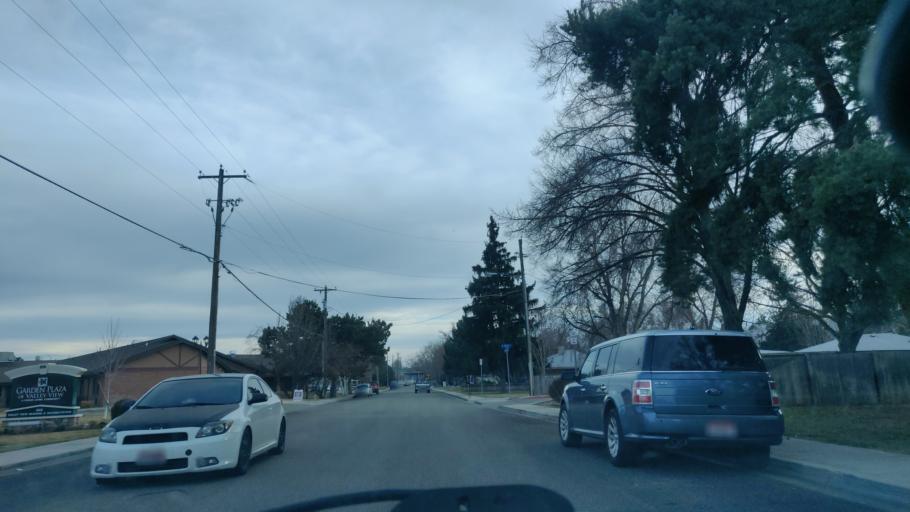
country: US
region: Idaho
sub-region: Ada County
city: Garden City
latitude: 43.6154
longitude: -116.2662
